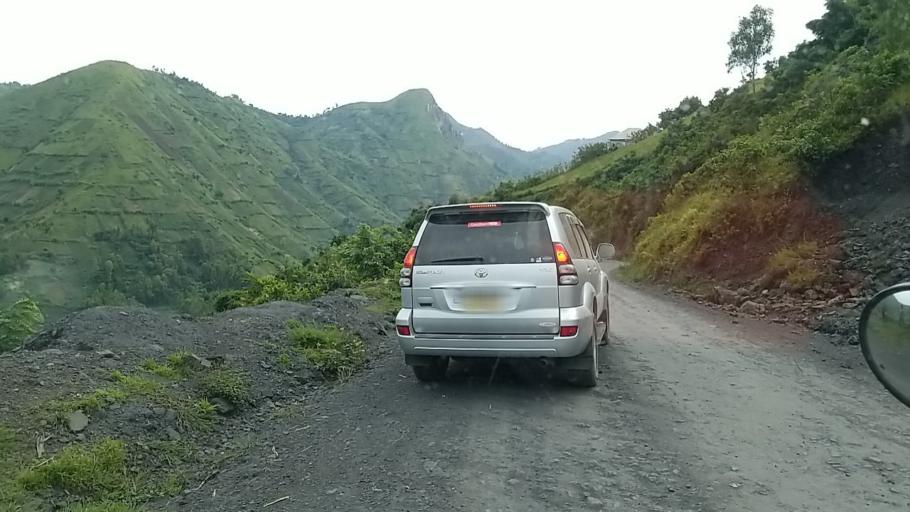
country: CD
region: Nord Kivu
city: Sake
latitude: -1.7602
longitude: 28.9901
